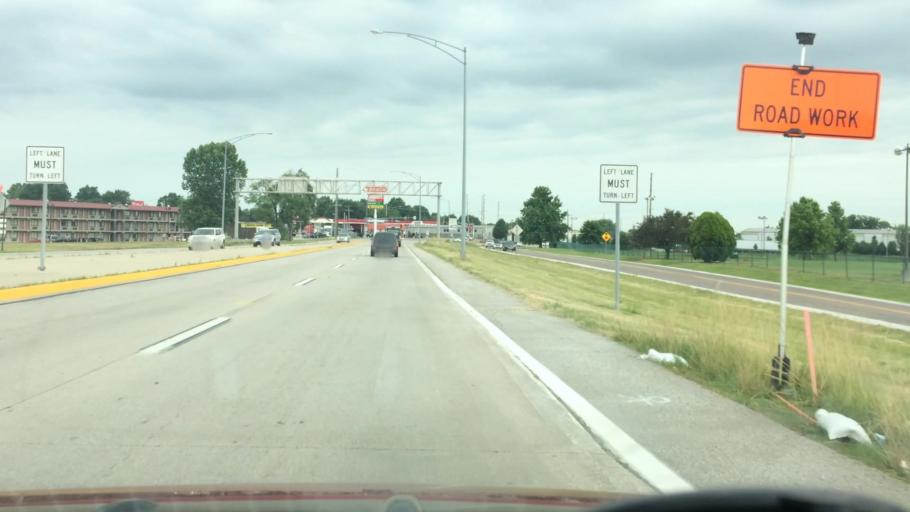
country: US
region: Missouri
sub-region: Greene County
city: Springfield
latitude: 37.2521
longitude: -93.2636
